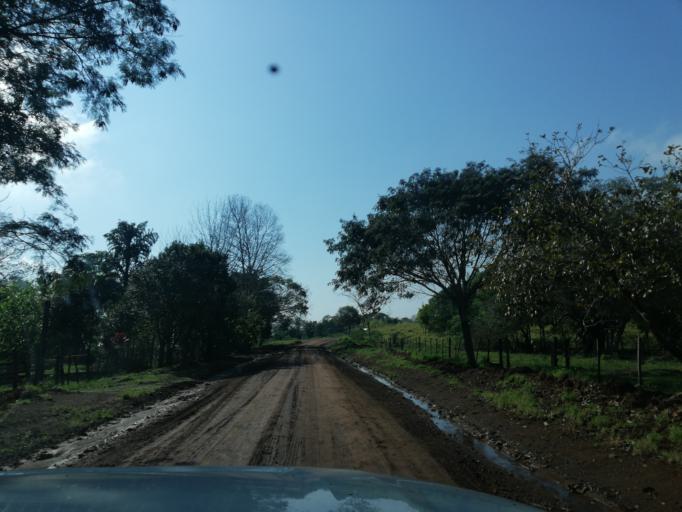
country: AR
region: Misiones
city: Cerro Azul
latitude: -27.6307
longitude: -55.5104
